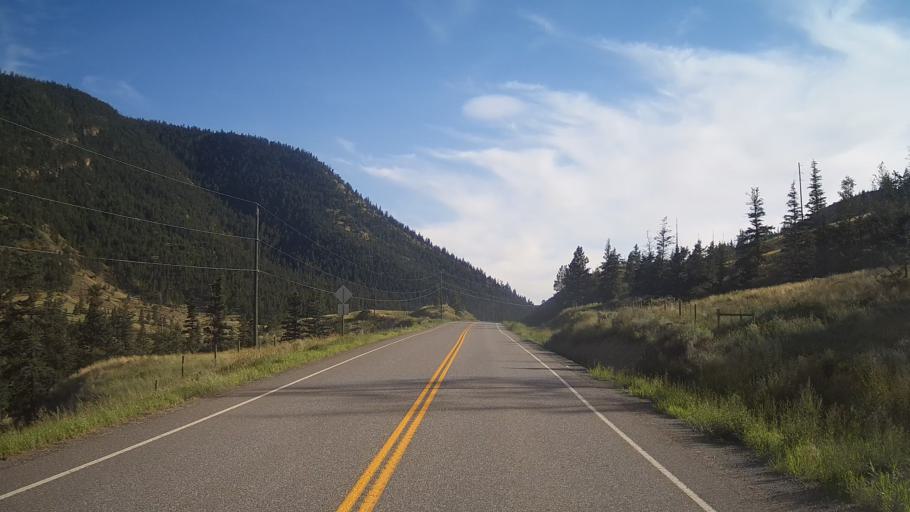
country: CA
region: British Columbia
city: Cache Creek
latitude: 50.8807
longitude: -121.5086
